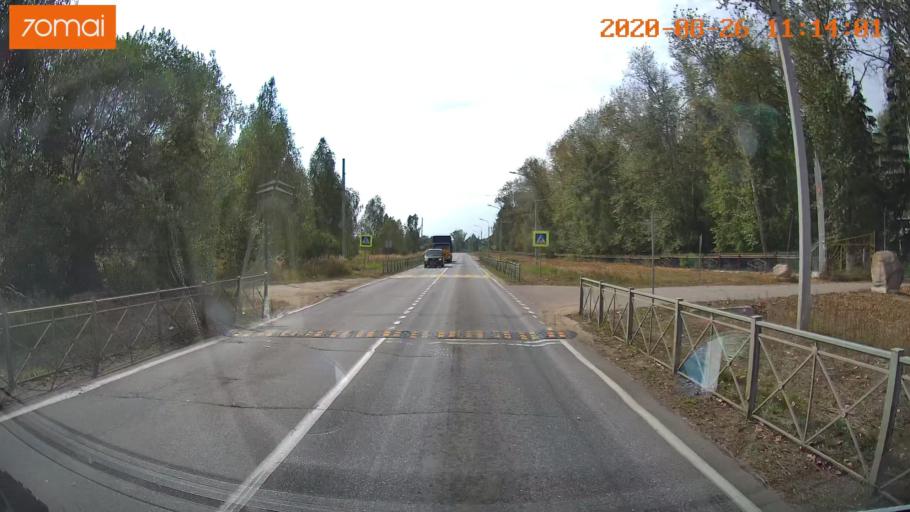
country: RU
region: Rjazan
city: Izhevskoye
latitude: 54.4520
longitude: 41.1182
